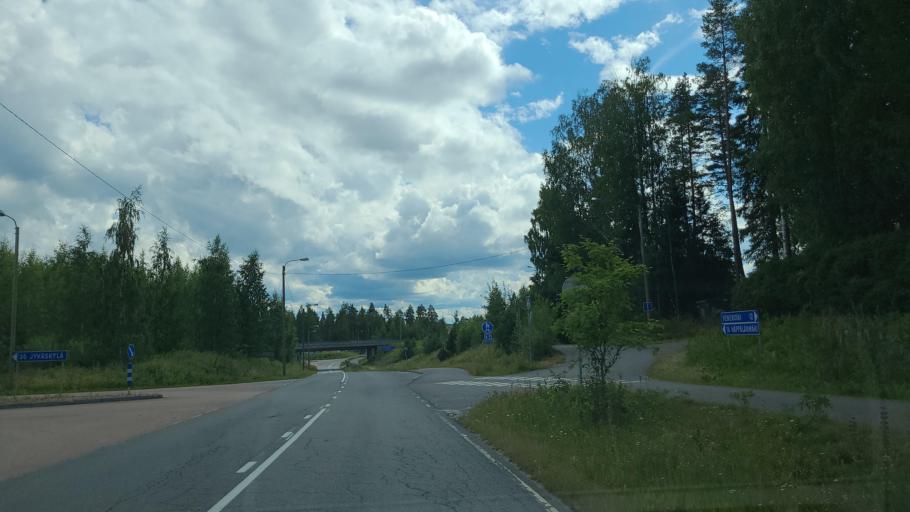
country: FI
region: Central Finland
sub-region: Jyvaeskylae
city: Hankasalmi
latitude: 62.2860
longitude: 26.3446
